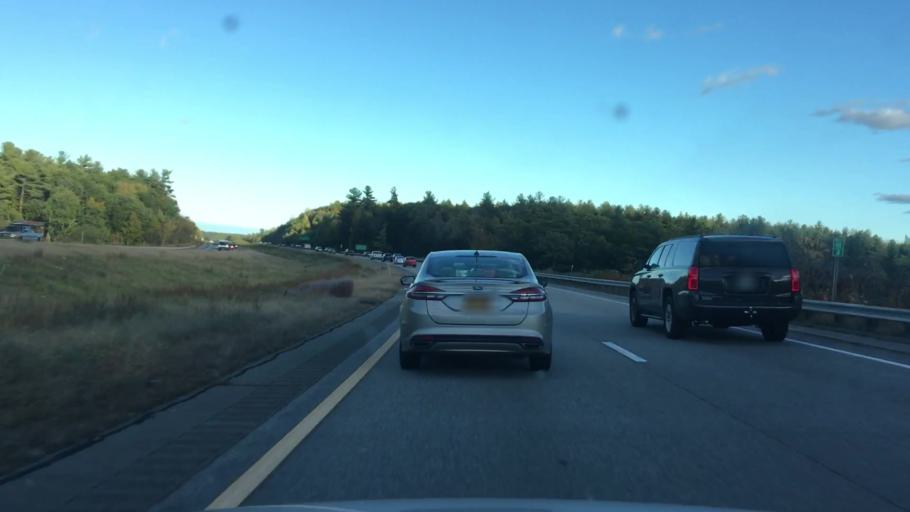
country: US
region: New Hampshire
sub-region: Rockingham County
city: Raymond
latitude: 43.0219
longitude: -71.2283
